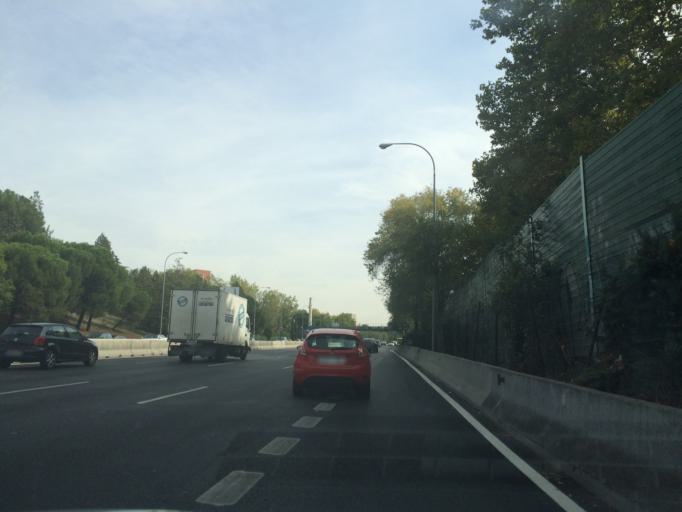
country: ES
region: Madrid
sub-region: Provincia de Madrid
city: Moncloa-Aravaca
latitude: 40.4506
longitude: -3.7398
